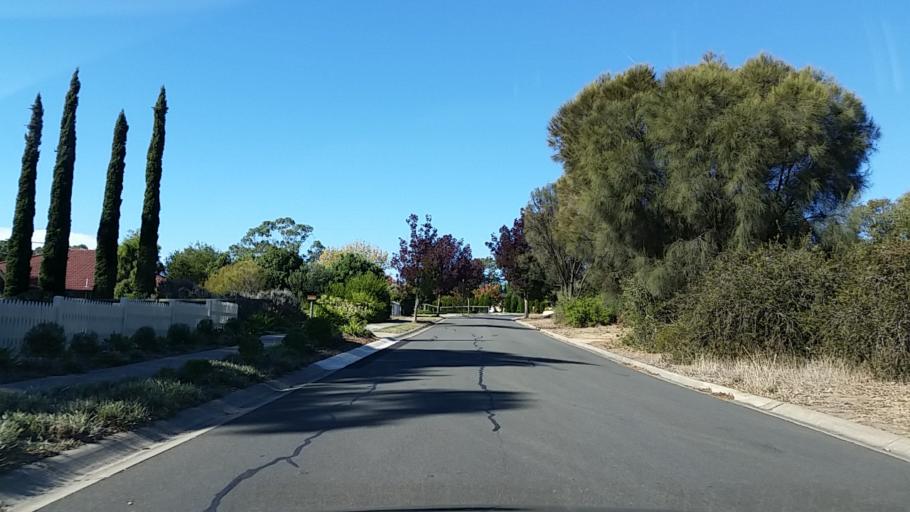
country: AU
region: South Australia
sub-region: Mount Barker
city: Mount Barker
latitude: -35.0583
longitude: 138.8788
